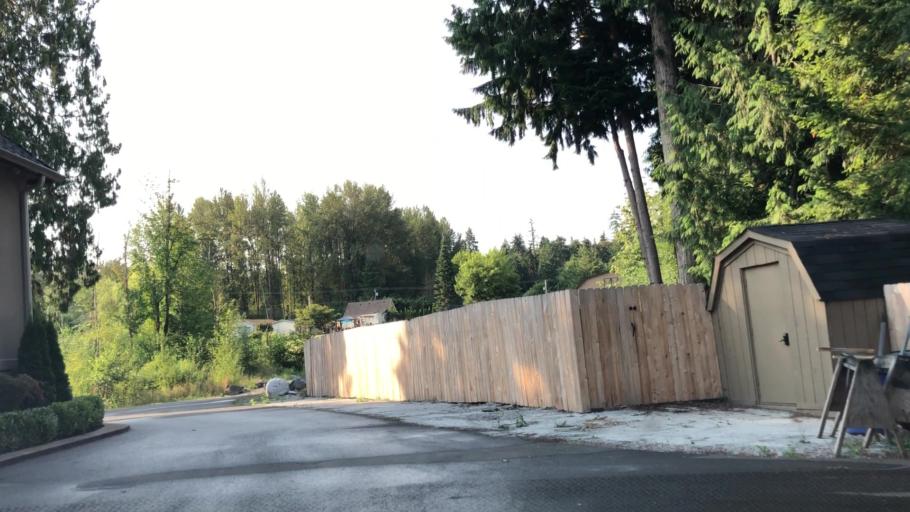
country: US
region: Washington
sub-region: King County
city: Cottage Lake
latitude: 47.7203
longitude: -122.0679
